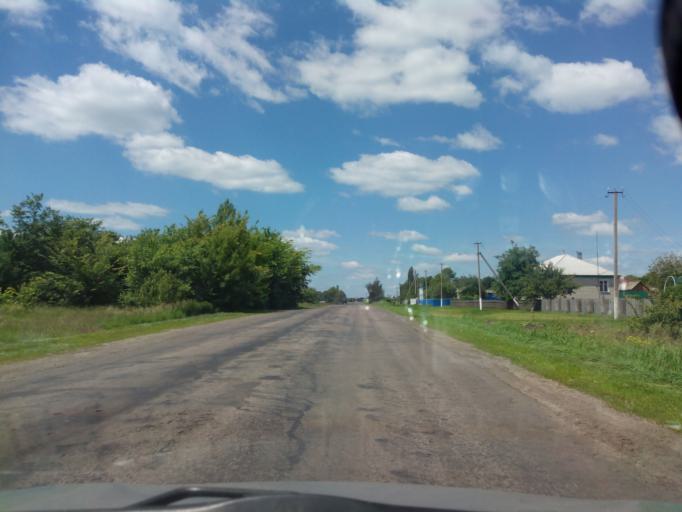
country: RU
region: Voronezj
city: Ternovka
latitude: 51.6702
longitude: 41.6365
